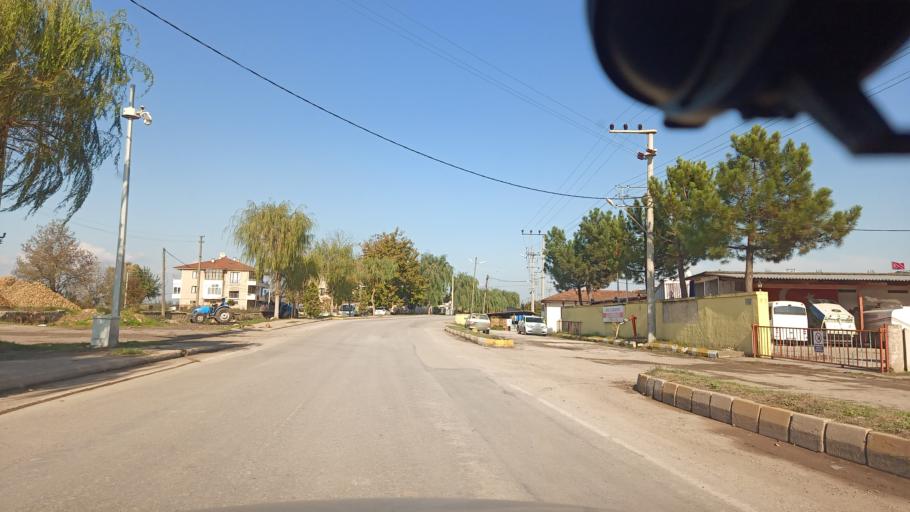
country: TR
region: Sakarya
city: Sogutlu
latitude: 40.8908
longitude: 30.4663
